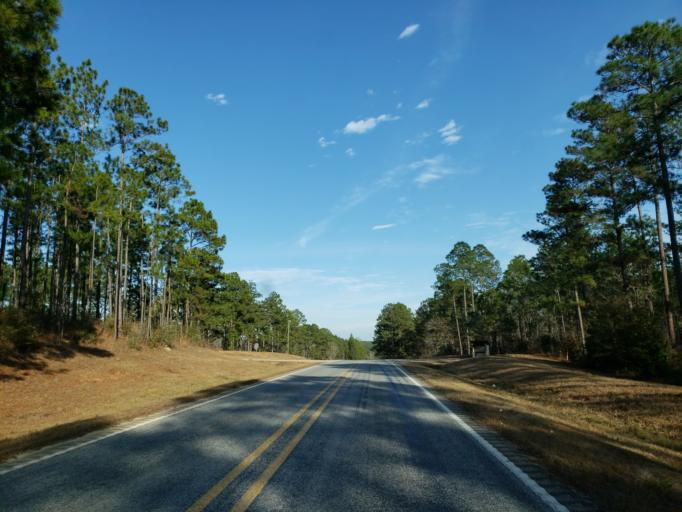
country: US
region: Mississippi
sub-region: Wayne County
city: Belmont
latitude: 31.3901
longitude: -88.6661
